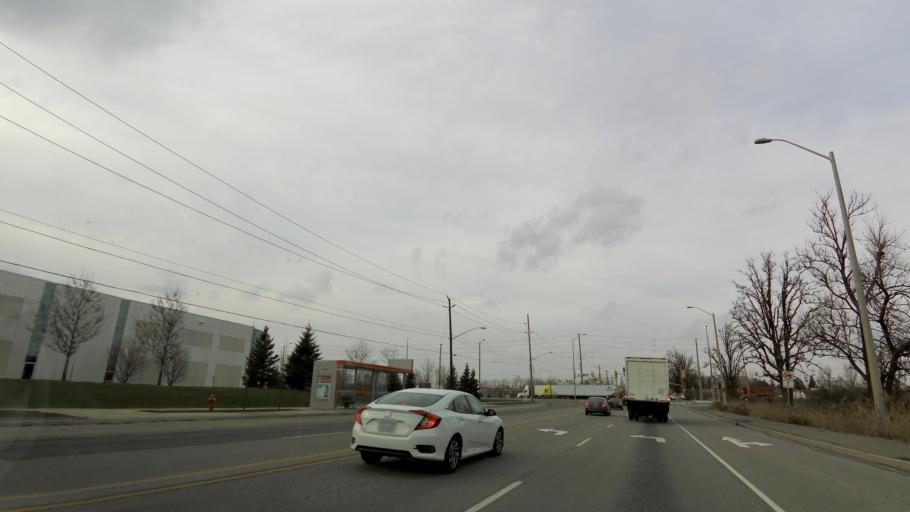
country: CA
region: Ontario
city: Etobicoke
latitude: 43.7419
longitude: -79.6462
